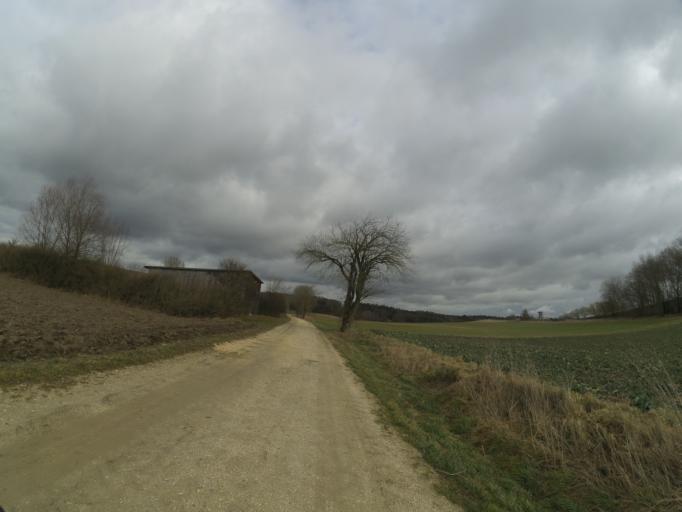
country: DE
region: Bavaria
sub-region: Swabia
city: Bellenberg
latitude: 48.2640
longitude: 10.1075
